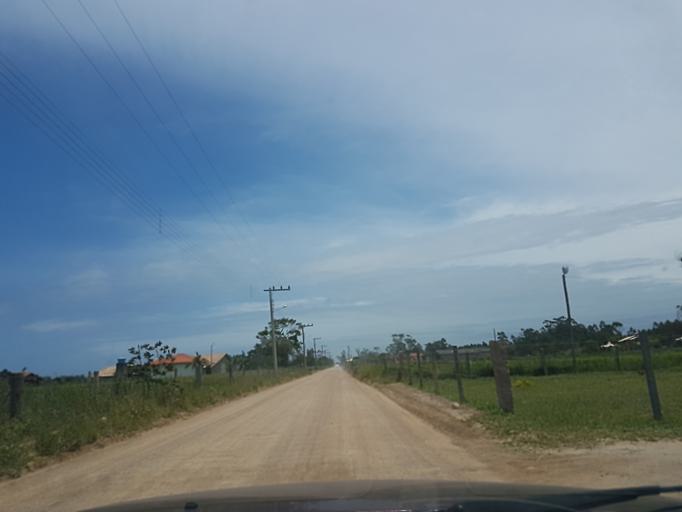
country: BR
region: Santa Catarina
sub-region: Jaguaruna
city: Jaguaruna
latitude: -28.6332
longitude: -48.9555
